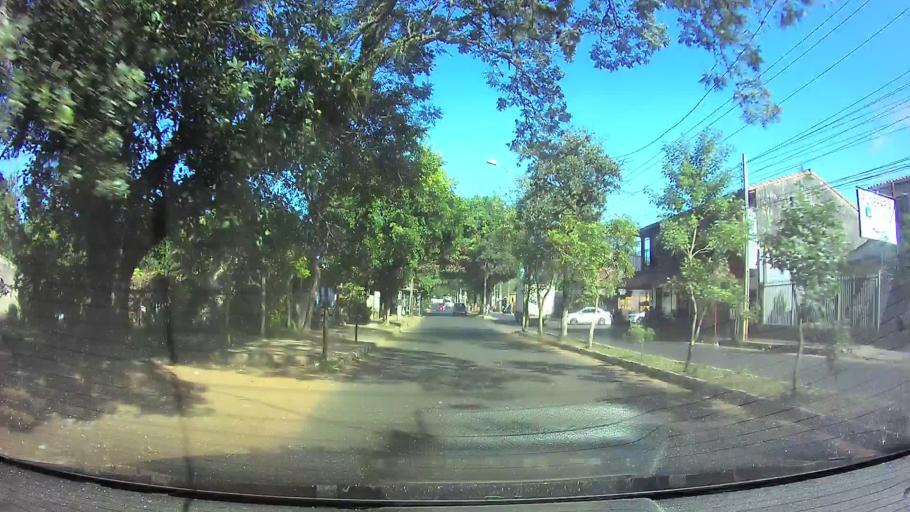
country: PY
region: Central
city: Villa Elisa
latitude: -25.3596
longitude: -57.5738
